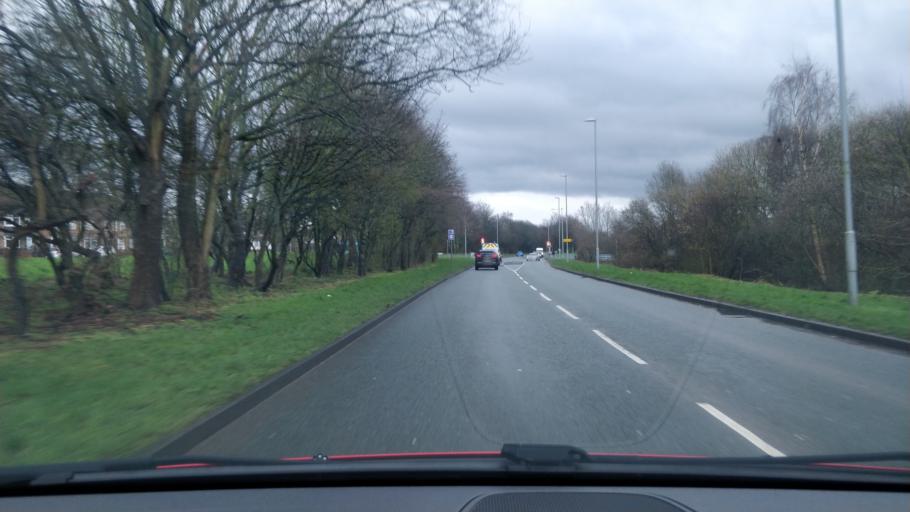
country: GB
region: England
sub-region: Knowsley
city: Huyton
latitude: 53.4256
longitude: -2.8512
